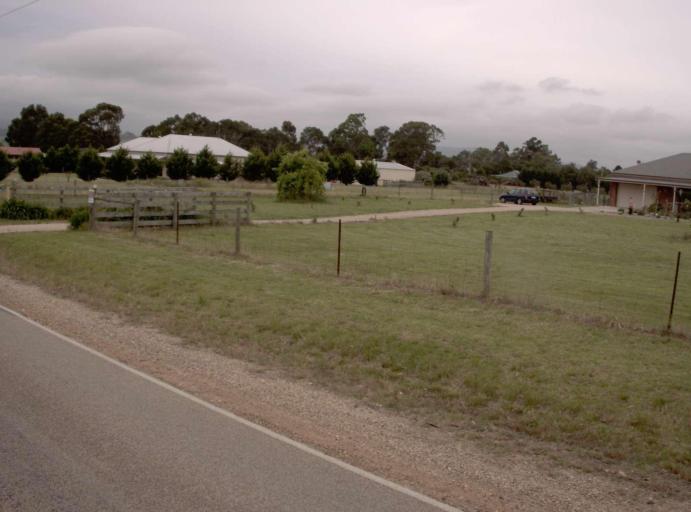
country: AU
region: Victoria
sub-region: East Gippsland
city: Bairnsdale
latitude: -37.8032
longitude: 147.4390
